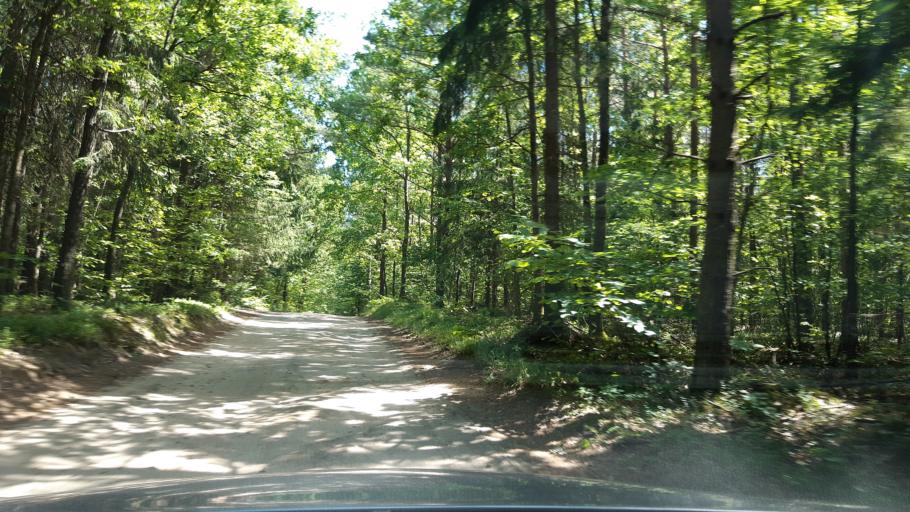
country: PL
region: Warmian-Masurian Voivodeship
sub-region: Powiat piski
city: Ruciane-Nida
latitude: 53.7125
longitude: 21.4960
